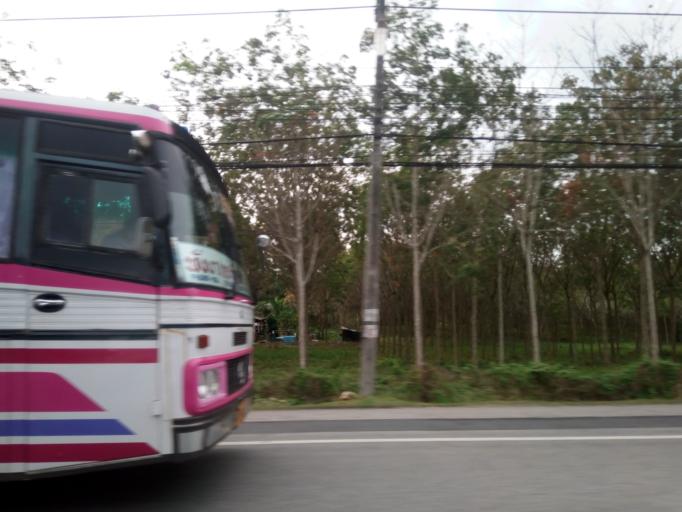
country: TH
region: Phuket
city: Thalang
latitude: 8.0529
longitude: 98.3384
